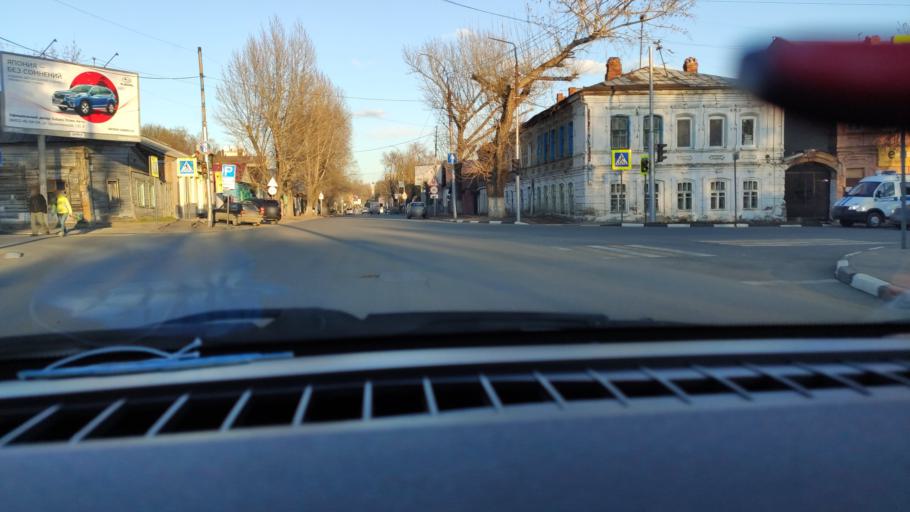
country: RU
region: Saratov
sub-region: Saratovskiy Rayon
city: Saratov
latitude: 51.5400
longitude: 46.0405
